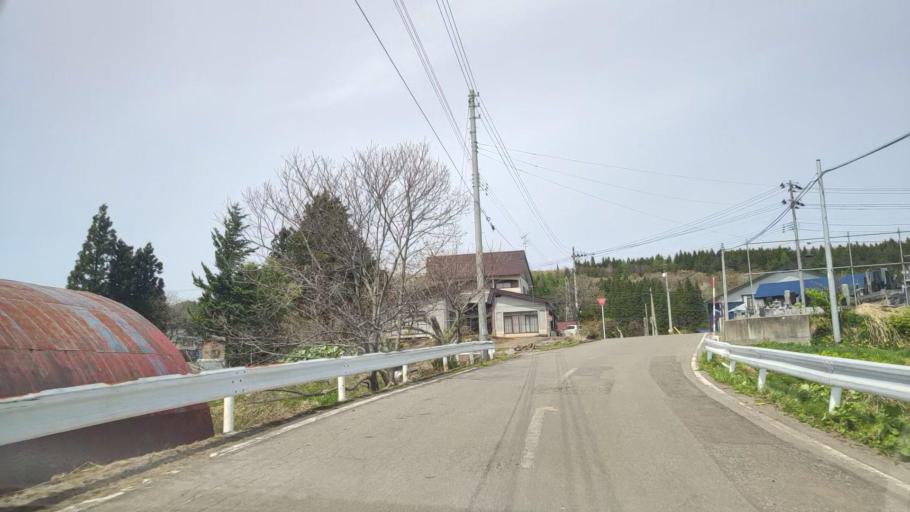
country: JP
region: Aomori
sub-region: Misawa Shi
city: Inuotose
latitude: 40.7885
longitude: 141.1094
